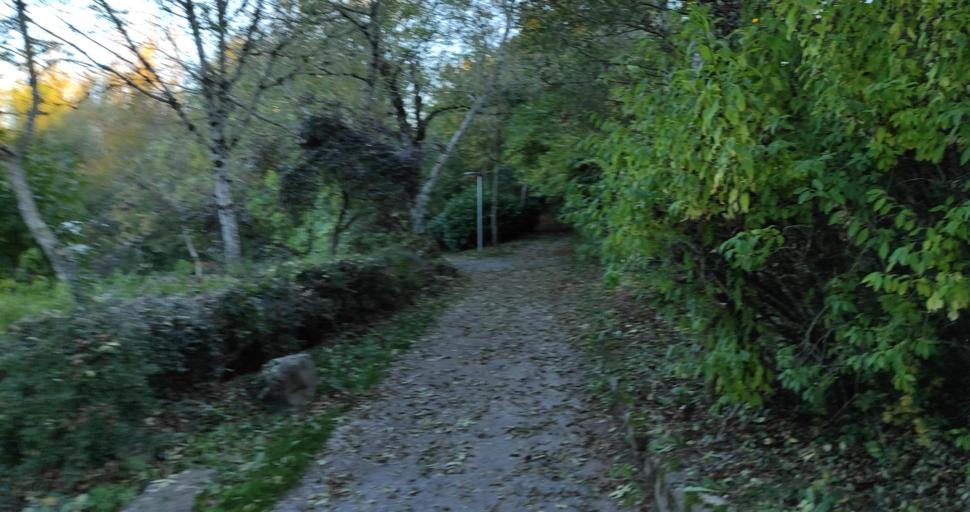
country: FR
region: Midi-Pyrenees
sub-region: Departement de l'Aveyron
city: Le Monastere
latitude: 44.3315
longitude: 2.5923
